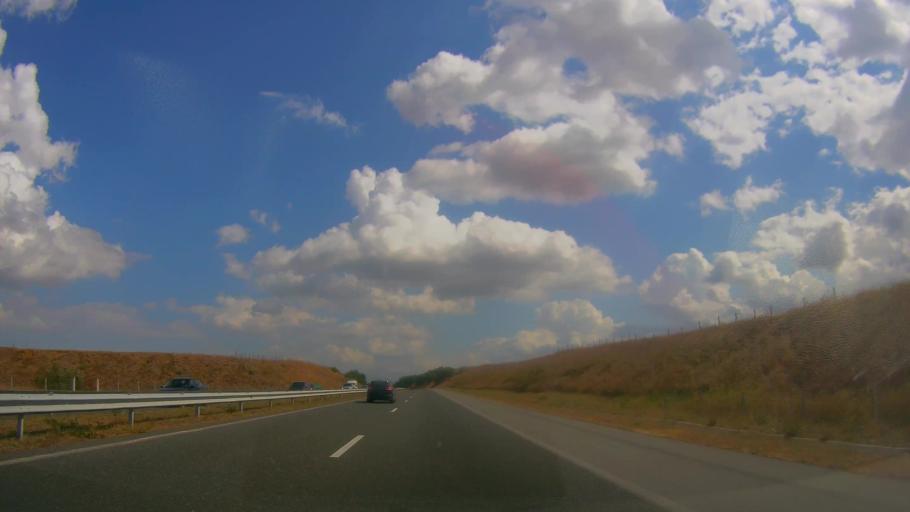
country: BG
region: Yambol
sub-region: Obshtina Yambol
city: Yambol
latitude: 42.5415
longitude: 26.4648
